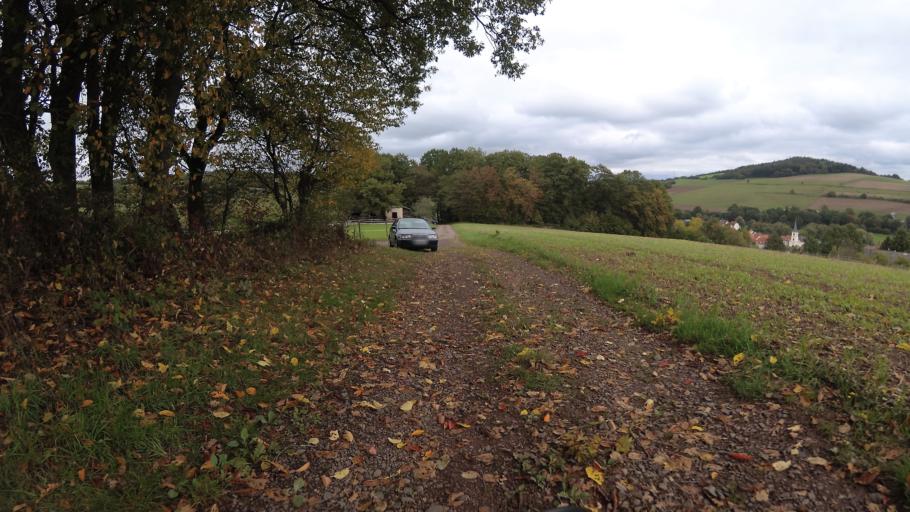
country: DE
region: Rheinland-Pfalz
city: Breitenbach
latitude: 49.4503
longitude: 7.2256
